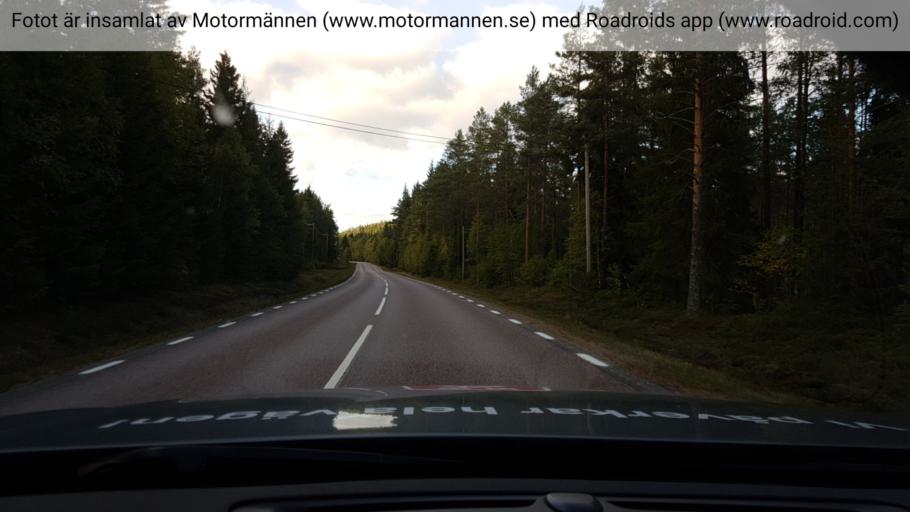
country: SE
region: Vaermland
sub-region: Filipstads Kommun
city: Lesjofors
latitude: 59.9879
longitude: 13.9709
